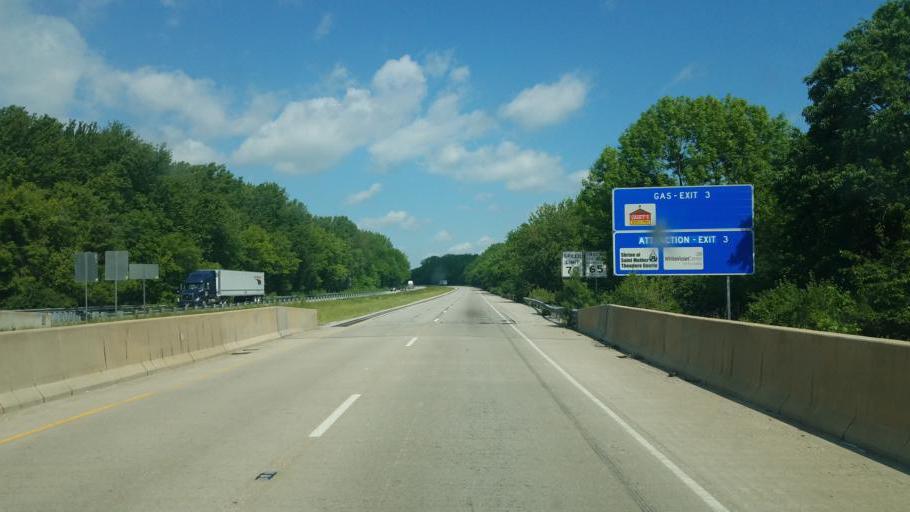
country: US
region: Indiana
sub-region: Vigo County
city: West Terre Haute
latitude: 39.4434
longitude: -87.4384
